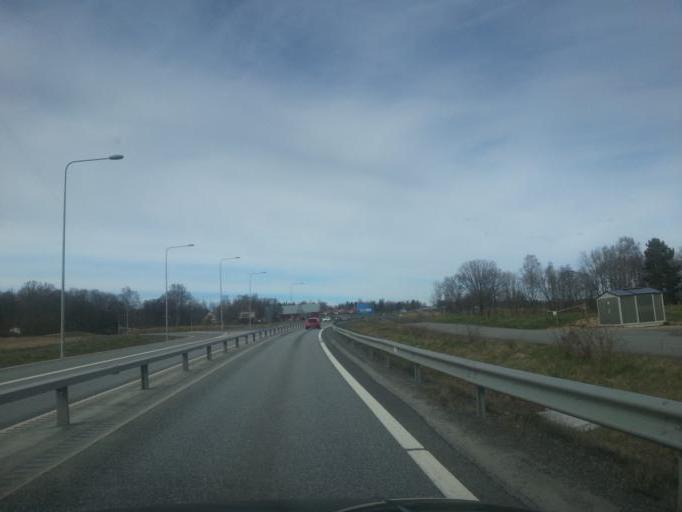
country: SE
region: Joenkoeping
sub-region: Jonkopings Kommun
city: Bankeryd
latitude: 57.8848
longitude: 14.1030
